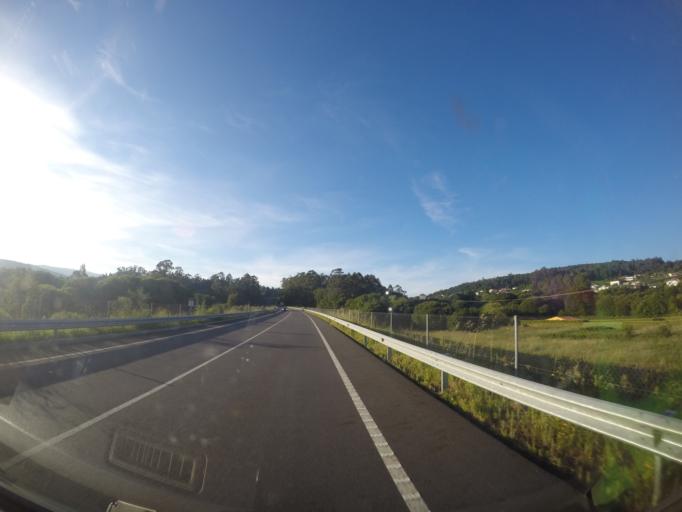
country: ES
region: Galicia
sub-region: Provincia da Coruna
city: Noia
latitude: 42.8044
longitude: -8.8888
